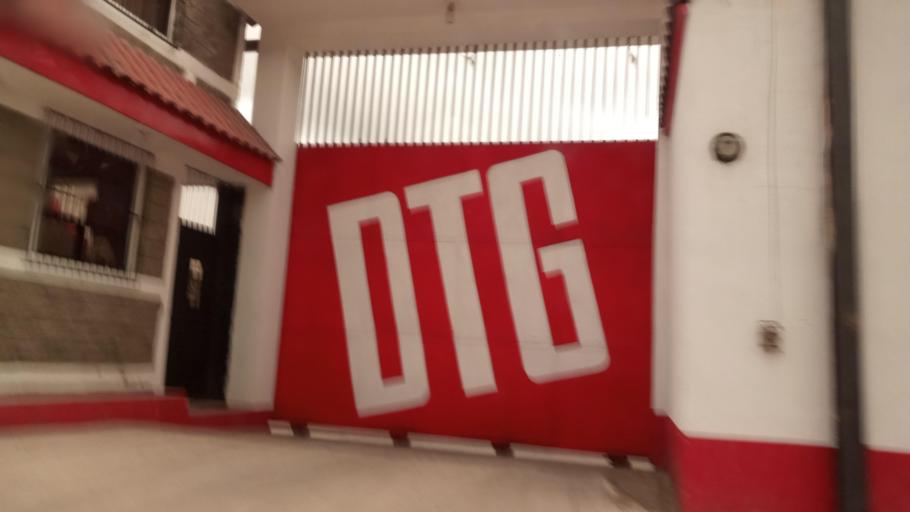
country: GT
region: Quetzaltenango
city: Quetzaltenango
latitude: 14.8257
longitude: -91.5342
